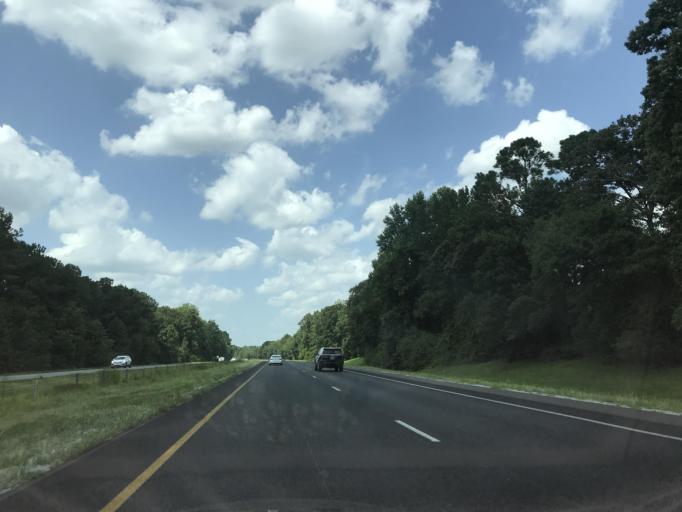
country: US
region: North Carolina
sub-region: Duplin County
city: Warsaw
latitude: 34.9401
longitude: -78.0570
